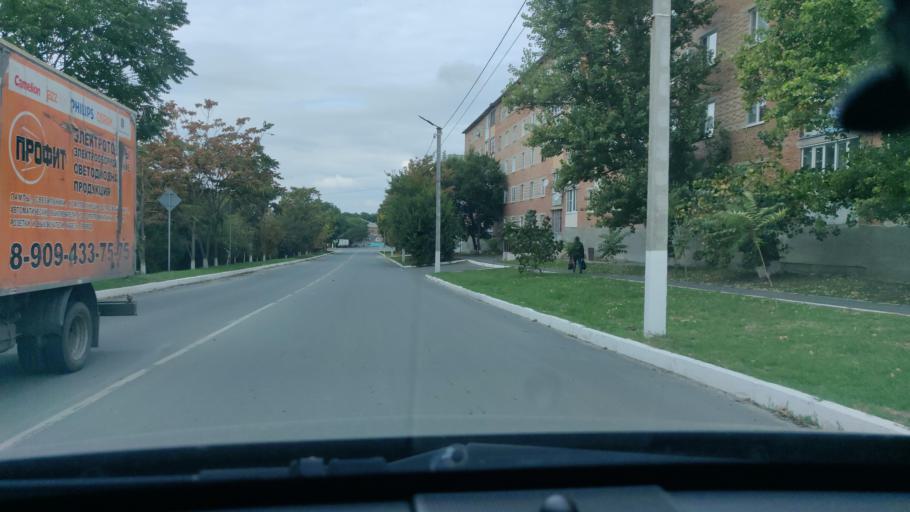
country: RU
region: Rostov
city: Ust'-Donetskiy
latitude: 47.6438
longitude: 40.8634
